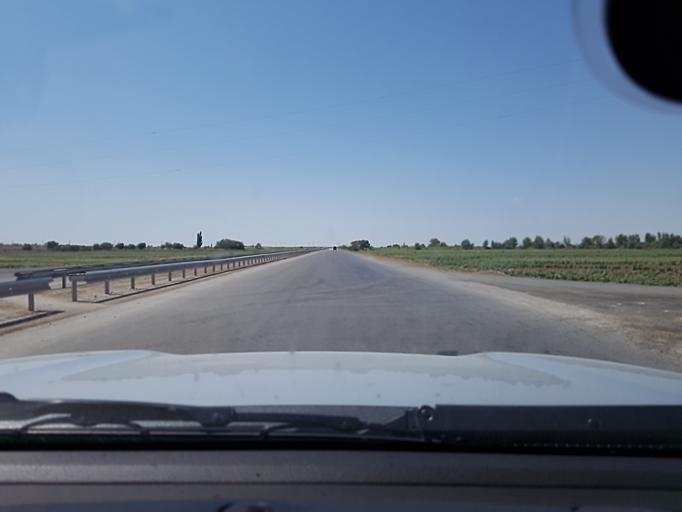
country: TM
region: Dasoguz
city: Yylanly
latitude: 41.7662
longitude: 59.4334
